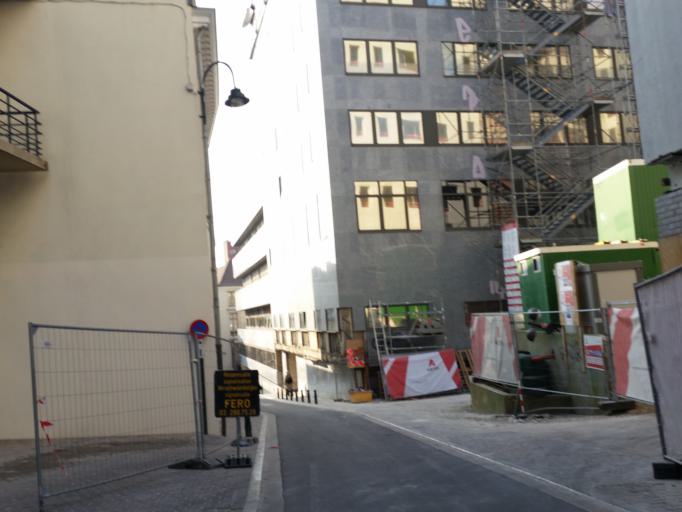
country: BE
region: Brussels Capital
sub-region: Bruxelles-Capitale
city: Brussels
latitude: 50.8427
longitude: 4.3498
